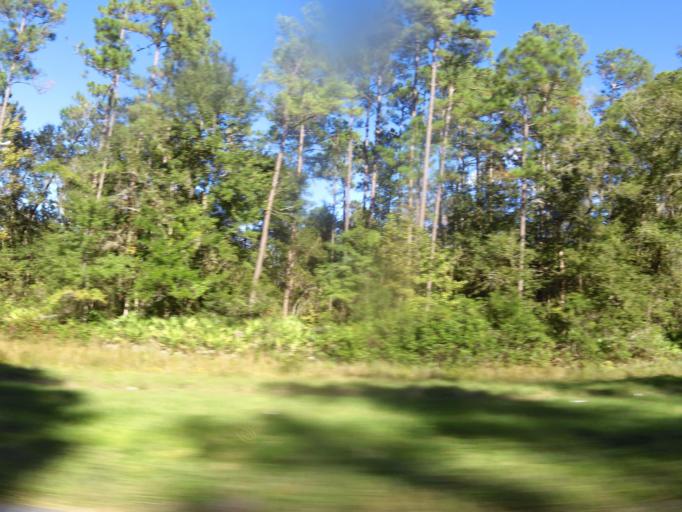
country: US
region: Florida
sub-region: Alachua County
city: Alachua
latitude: 29.7183
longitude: -82.3859
